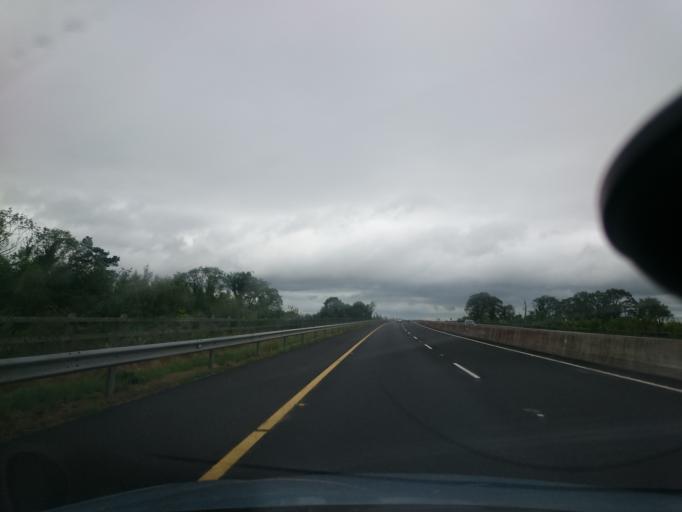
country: IE
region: Leinster
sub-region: Kildare
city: Moone
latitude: 52.9538
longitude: -6.8565
